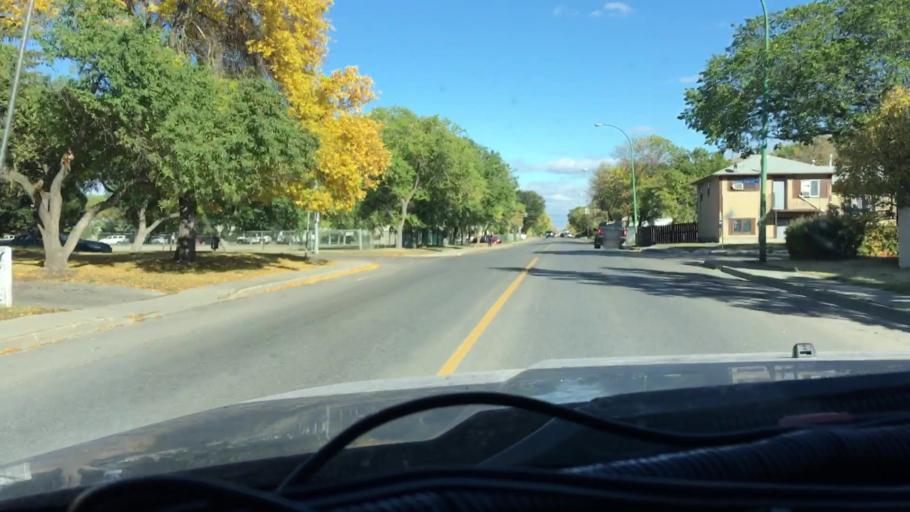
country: CA
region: Saskatchewan
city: Regina
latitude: 50.4629
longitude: -104.6274
